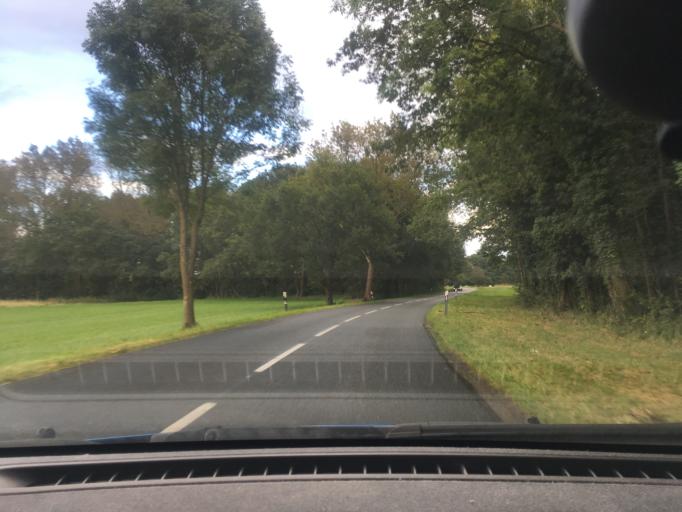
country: DE
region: Lower Saxony
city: Neu Darchau
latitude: 53.3263
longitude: 10.8944
